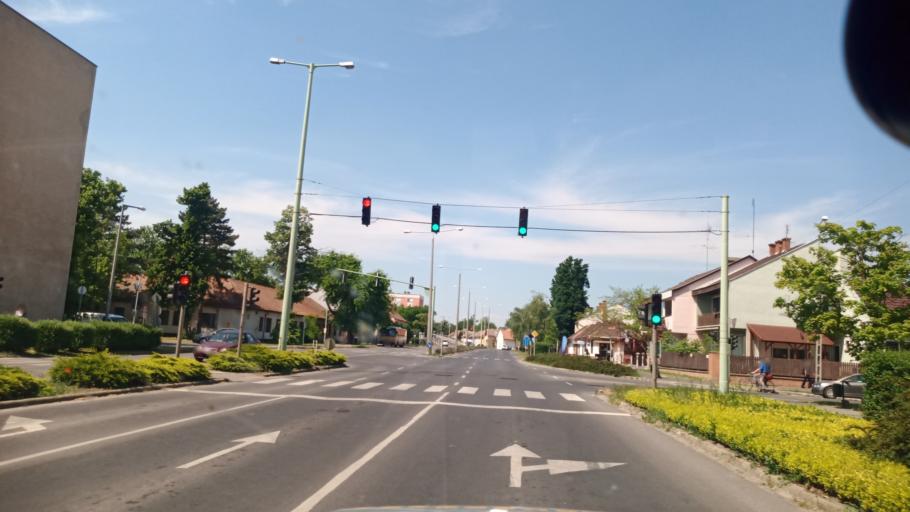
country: HU
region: Bekes
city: Oroshaza
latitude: 46.5594
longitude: 20.6624
